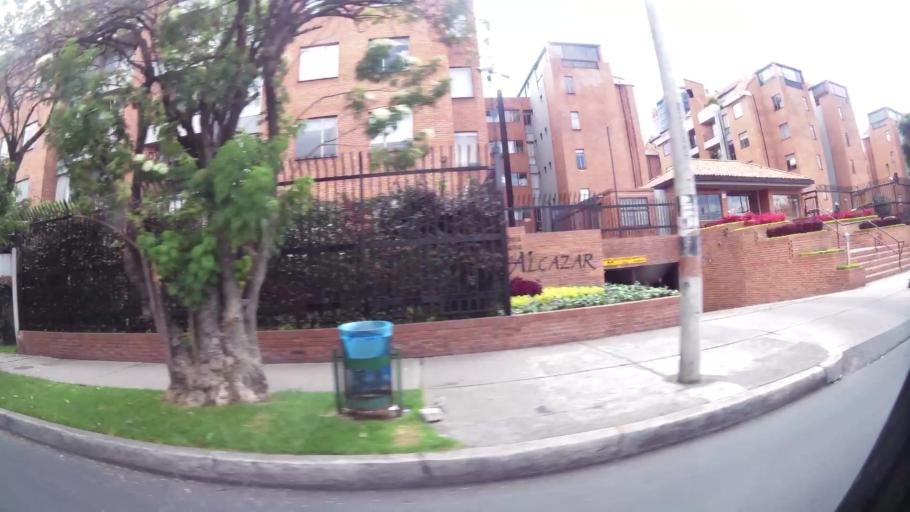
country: CO
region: Bogota D.C.
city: Barrio San Luis
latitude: 4.6979
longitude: -74.0579
